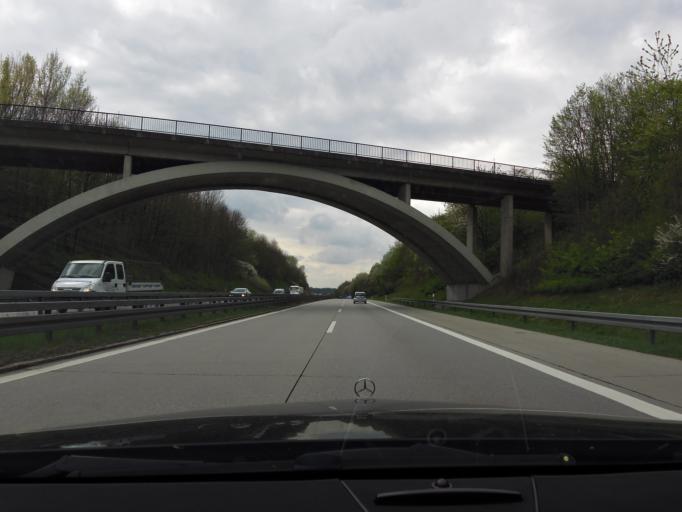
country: DE
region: Bavaria
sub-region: Lower Bavaria
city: Ergolding
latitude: 48.5699
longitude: 12.1126
